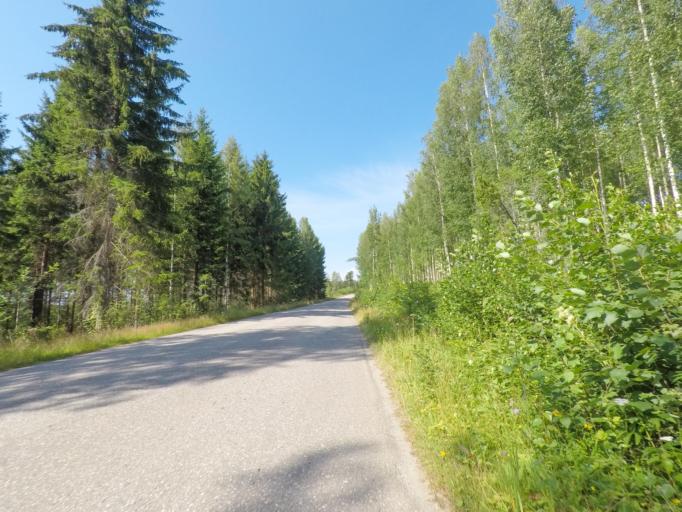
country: FI
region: Southern Savonia
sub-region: Mikkeli
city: Puumala
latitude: 61.4446
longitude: 28.1621
